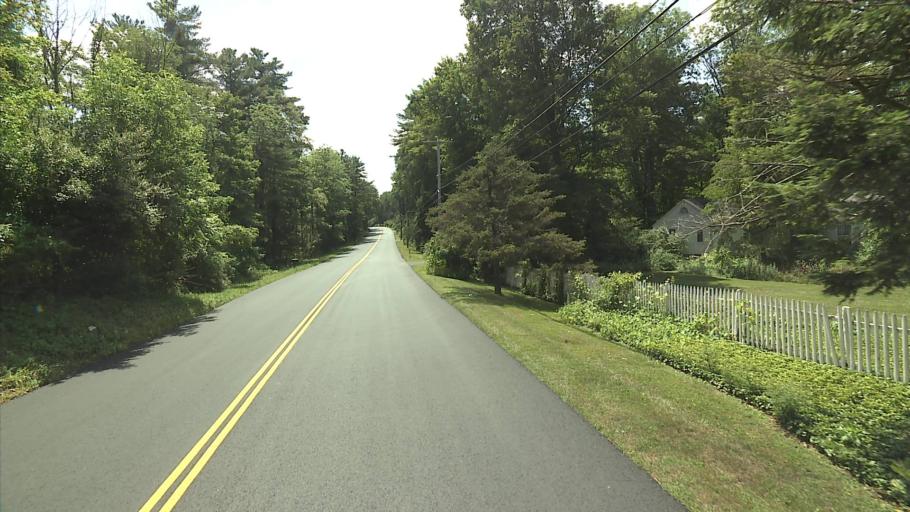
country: US
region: Connecticut
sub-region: Litchfield County
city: Canaan
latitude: 41.9955
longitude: -73.3606
